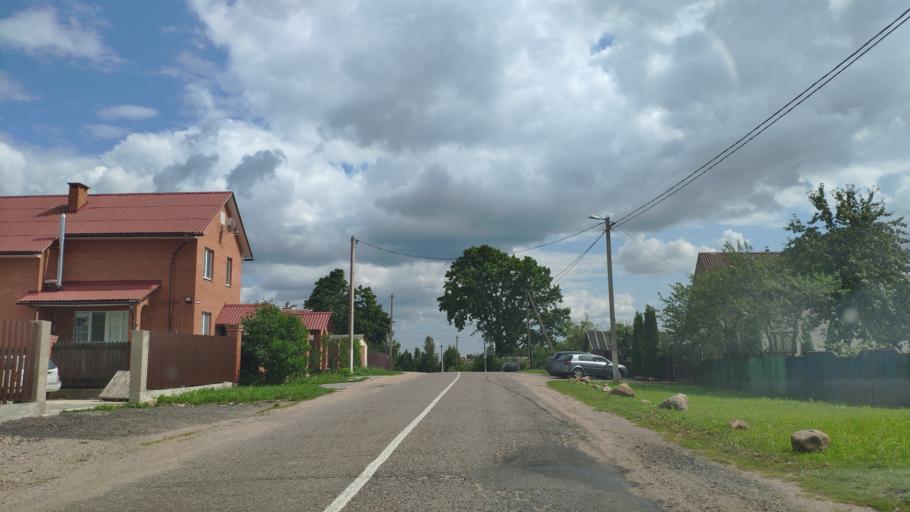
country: BY
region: Minsk
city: Khatsyezhyna
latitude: 53.8831
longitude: 27.2734
